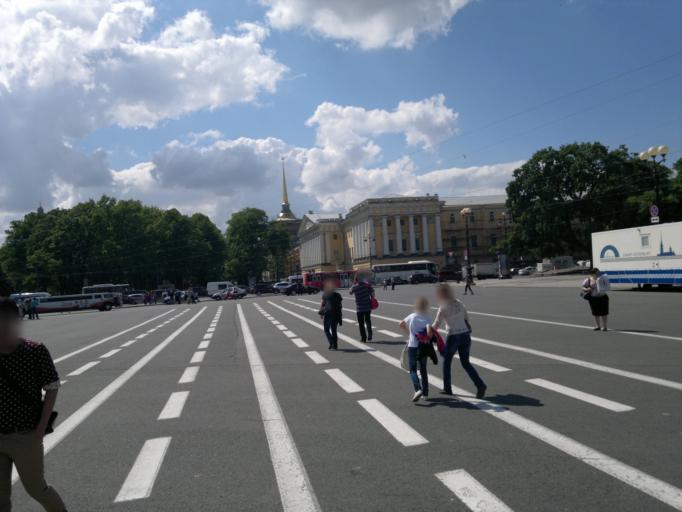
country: RU
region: St.-Petersburg
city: Saint Petersburg
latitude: 59.9389
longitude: 30.3137
